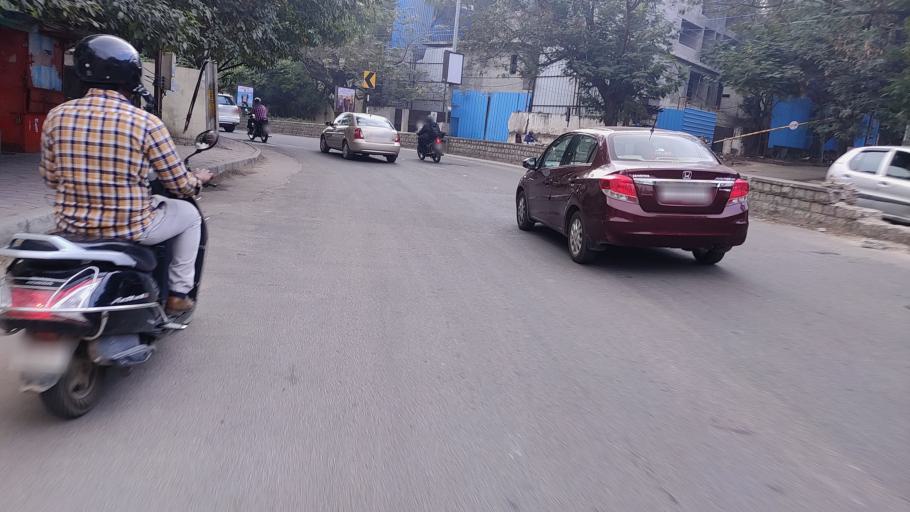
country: IN
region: Telangana
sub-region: Rangareddi
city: Kukatpalli
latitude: 17.4329
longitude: 78.4173
